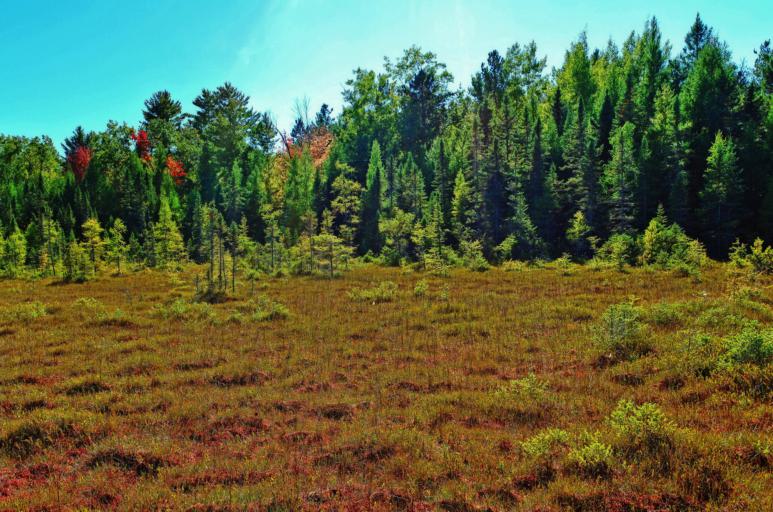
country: US
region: Wisconsin
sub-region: Sawyer County
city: Hayward
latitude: 46.0129
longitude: -91.5334
